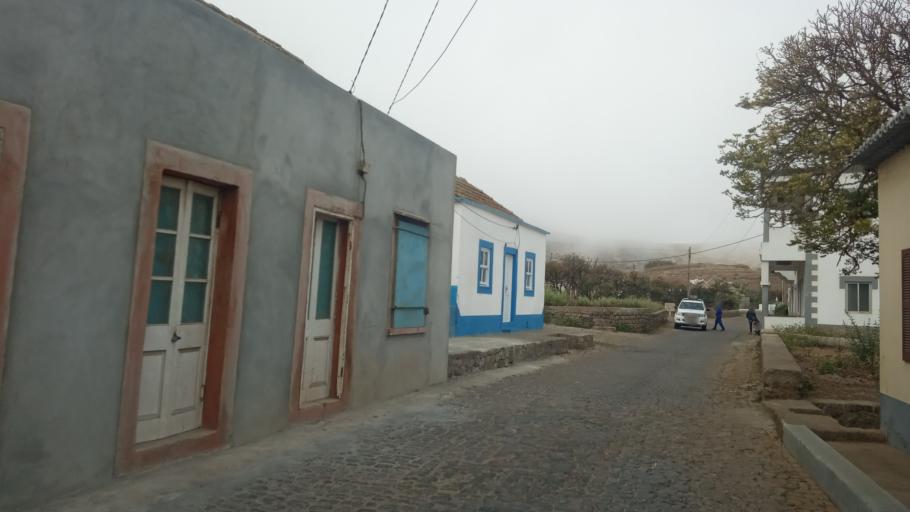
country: CV
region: Brava
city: Vila Nova Sintra
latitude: 14.8707
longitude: -24.7048
